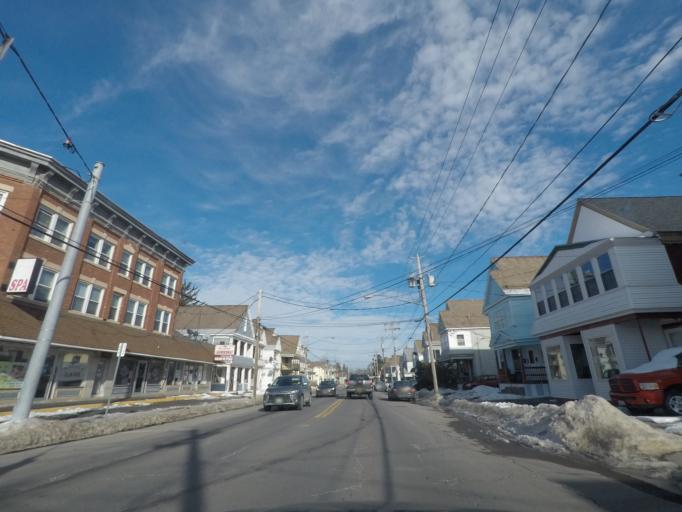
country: US
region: New York
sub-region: Schenectady County
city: Rotterdam
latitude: 42.7985
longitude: -73.9634
